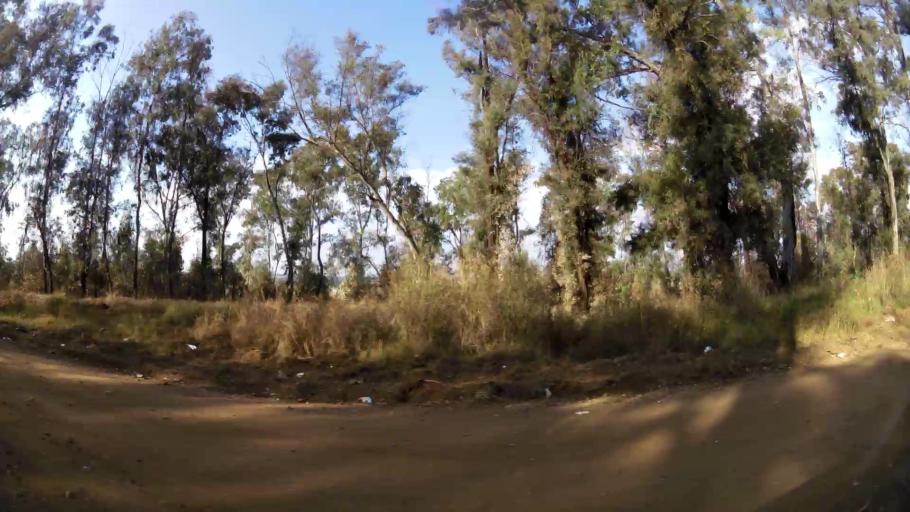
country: ZA
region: Gauteng
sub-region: Ekurhuleni Metropolitan Municipality
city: Tembisa
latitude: -25.9323
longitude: 28.2326
